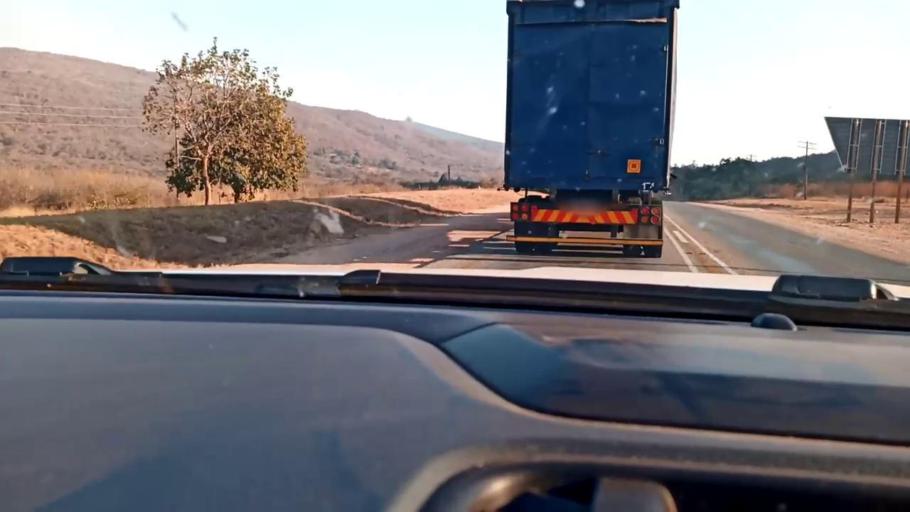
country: ZA
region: Limpopo
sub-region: Mopani District Municipality
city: Duiwelskloof
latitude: -23.6547
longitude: 30.1705
